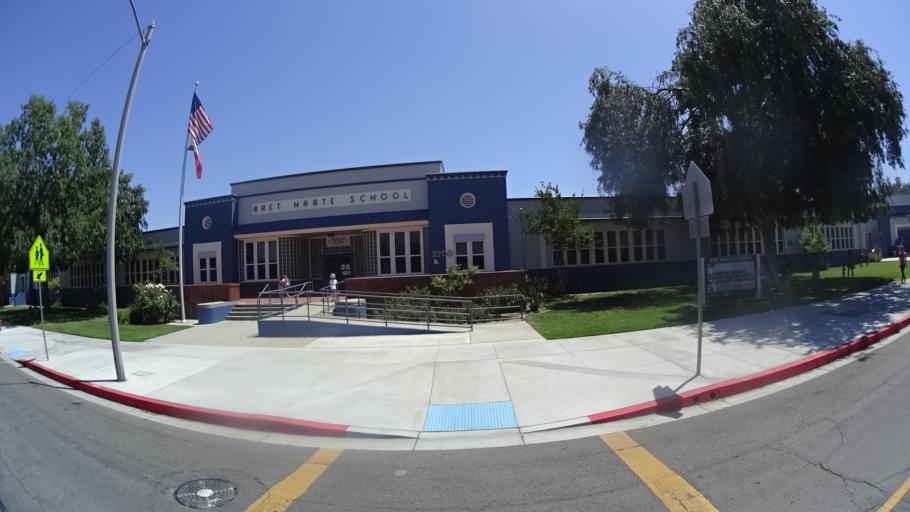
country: US
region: California
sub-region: Los Angeles County
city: North Hollywood
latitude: 34.1811
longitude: -118.3460
